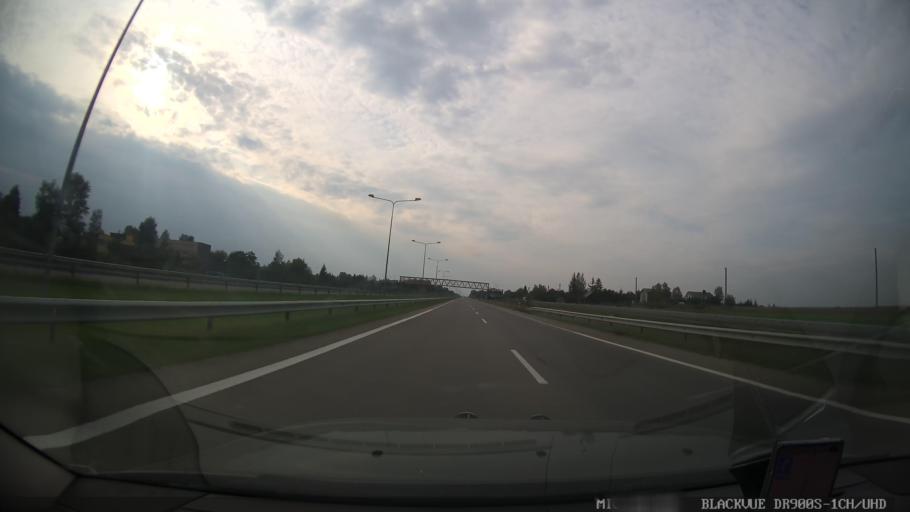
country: LT
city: Skaidiskes
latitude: 54.6402
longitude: 25.3611
